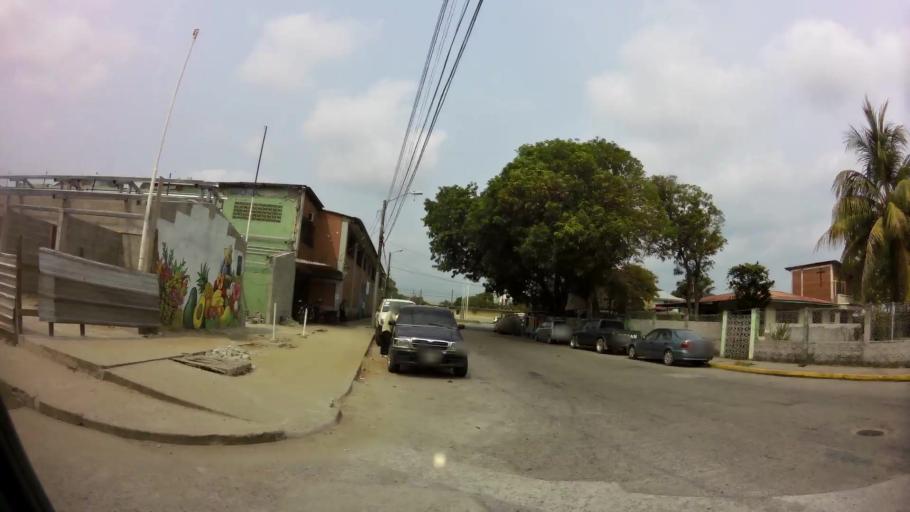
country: HN
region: Atlantida
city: Tela
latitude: 15.7841
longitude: -87.4520
